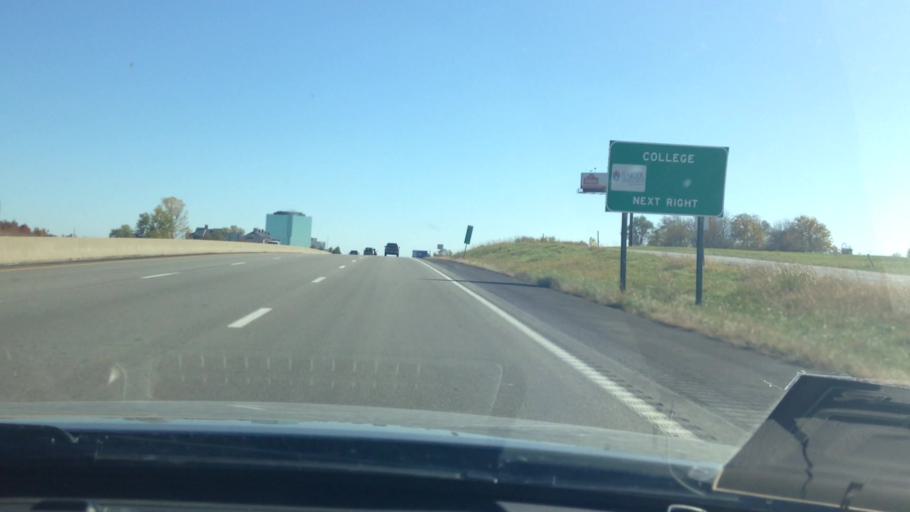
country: US
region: Missouri
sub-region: Platte County
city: Weatherby Lake
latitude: 39.2859
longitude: -94.6787
